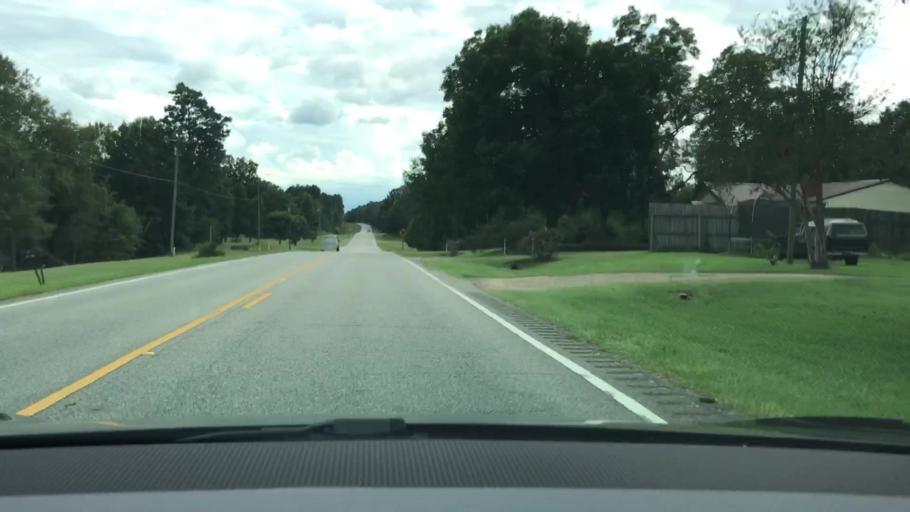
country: US
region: Alabama
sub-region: Pike County
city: Troy
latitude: 31.6482
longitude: -85.9695
